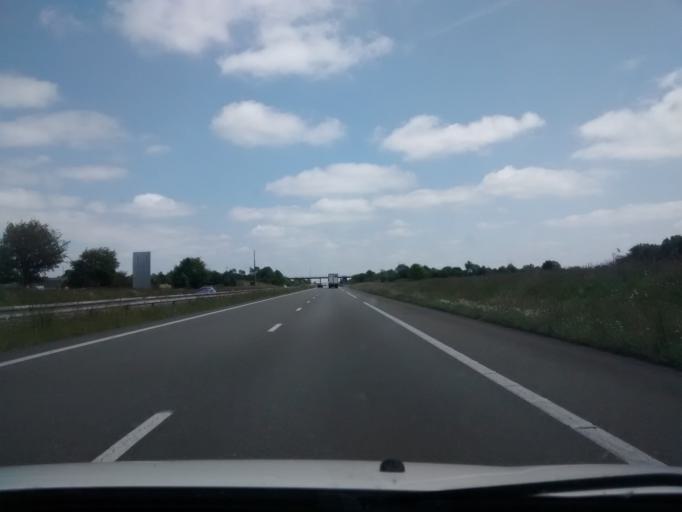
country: FR
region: Pays de la Loire
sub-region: Departement de la Mayenne
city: Soulge-sur-Ouette
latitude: 48.0718
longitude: -0.5760
